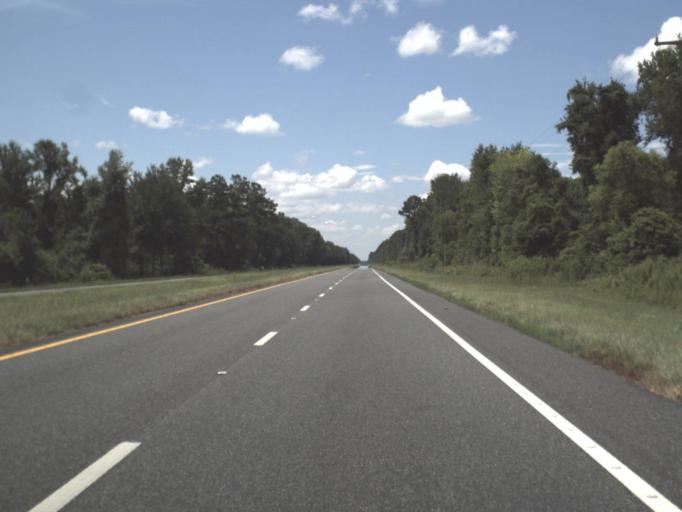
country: US
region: Florida
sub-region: Taylor County
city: Perry
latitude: 30.2654
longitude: -83.7137
